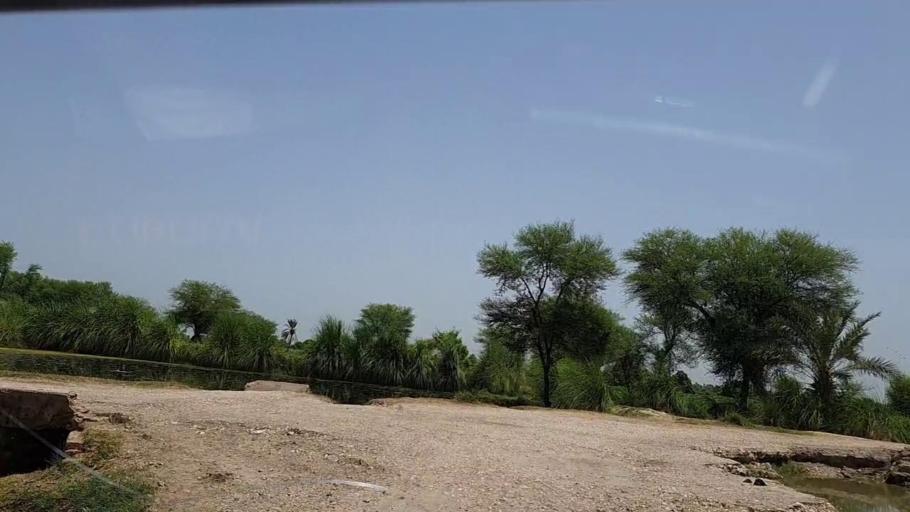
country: PK
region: Sindh
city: Tharu Shah
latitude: 26.9260
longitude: 68.0416
